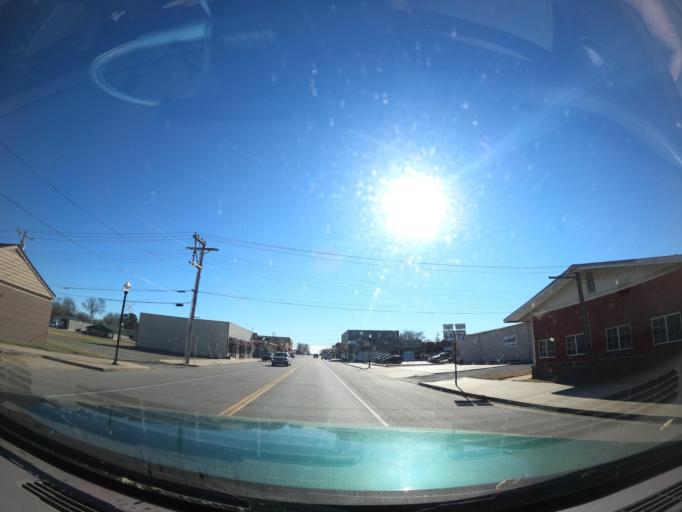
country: US
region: Oklahoma
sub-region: Muskogee County
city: Haskell
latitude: 35.8199
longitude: -95.6750
